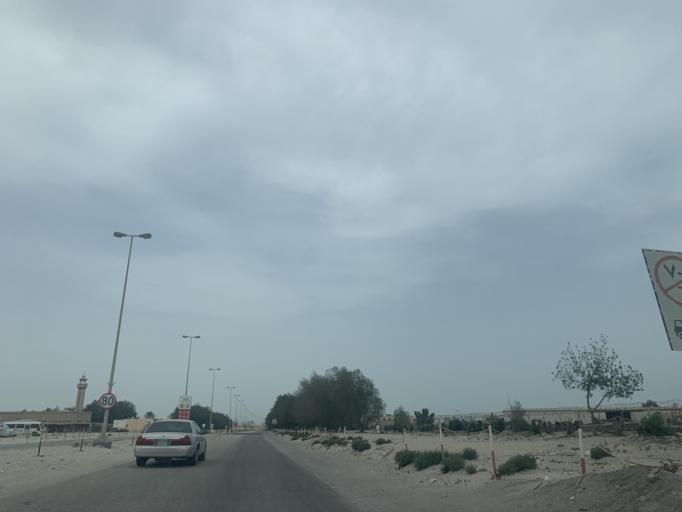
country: BH
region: Muharraq
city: Al Hadd
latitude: 26.1941
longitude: 50.6646
